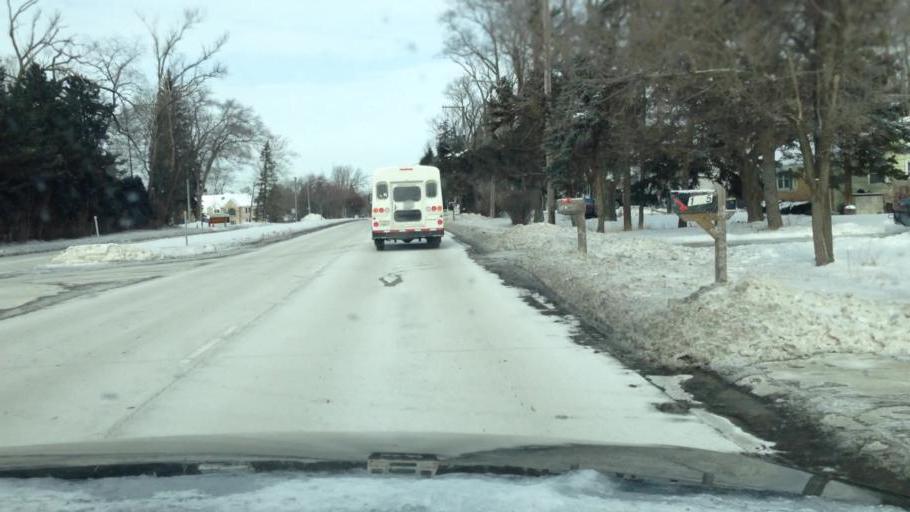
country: US
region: Illinois
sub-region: DuPage County
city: Lombard
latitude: 41.8508
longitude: -88.0118
